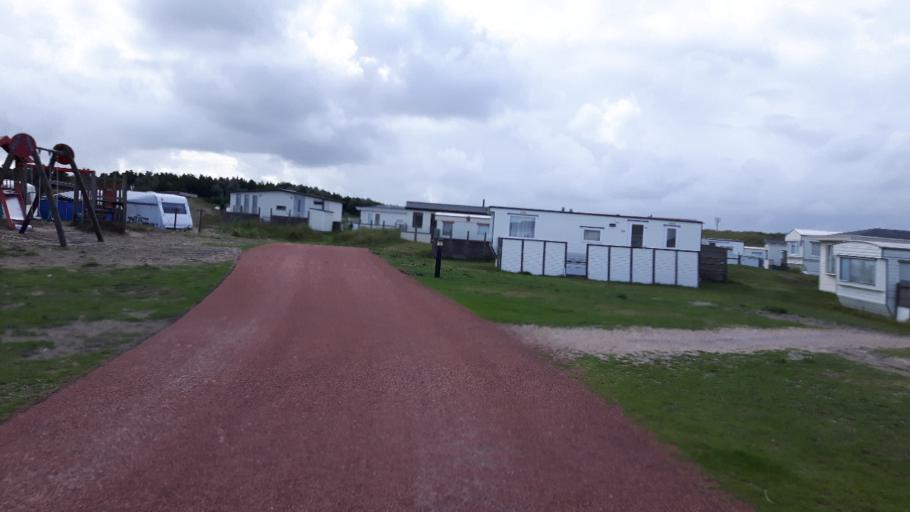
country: NL
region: Friesland
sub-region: Gemeente Ameland
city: Nes
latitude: 53.4573
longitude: 5.7691
